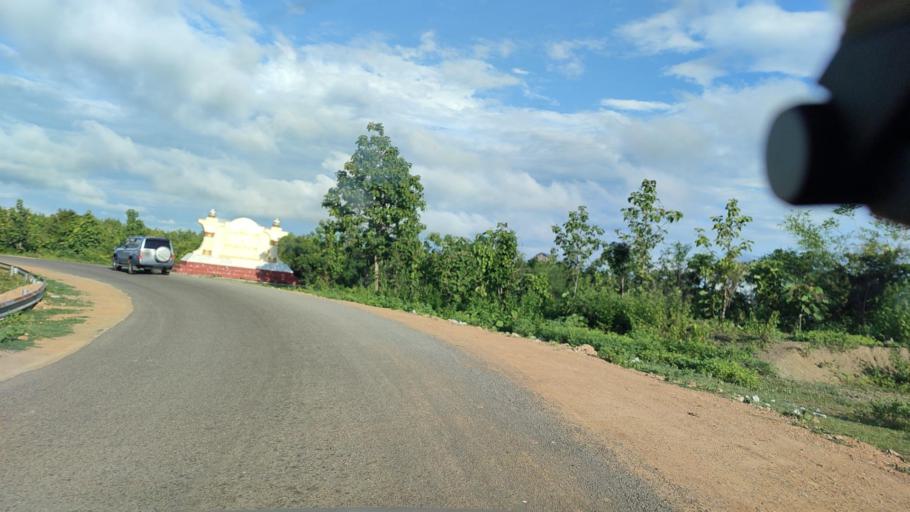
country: MM
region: Magway
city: Taungdwingyi
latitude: 20.0534
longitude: 95.7715
